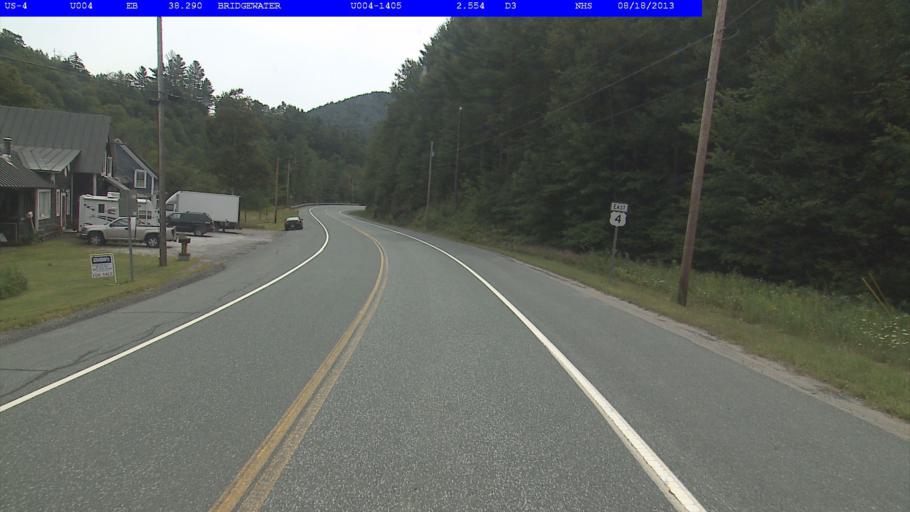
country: US
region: Vermont
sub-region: Windsor County
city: Woodstock
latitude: 43.5942
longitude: -72.7079
